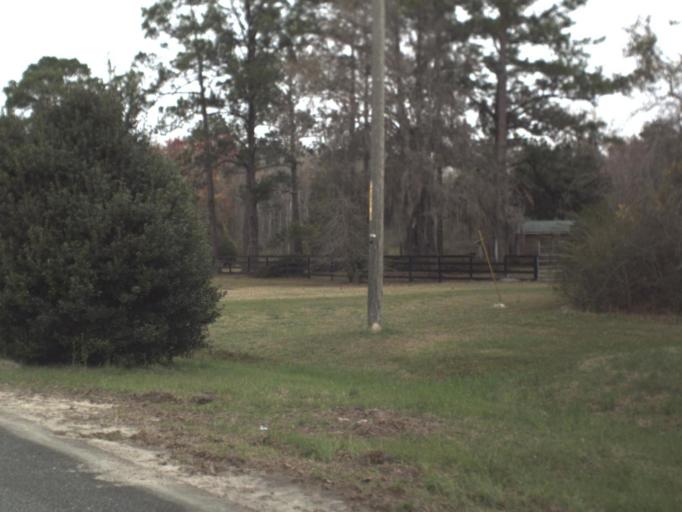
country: US
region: Florida
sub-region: Jefferson County
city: Monticello
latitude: 30.5072
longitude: -83.7693
